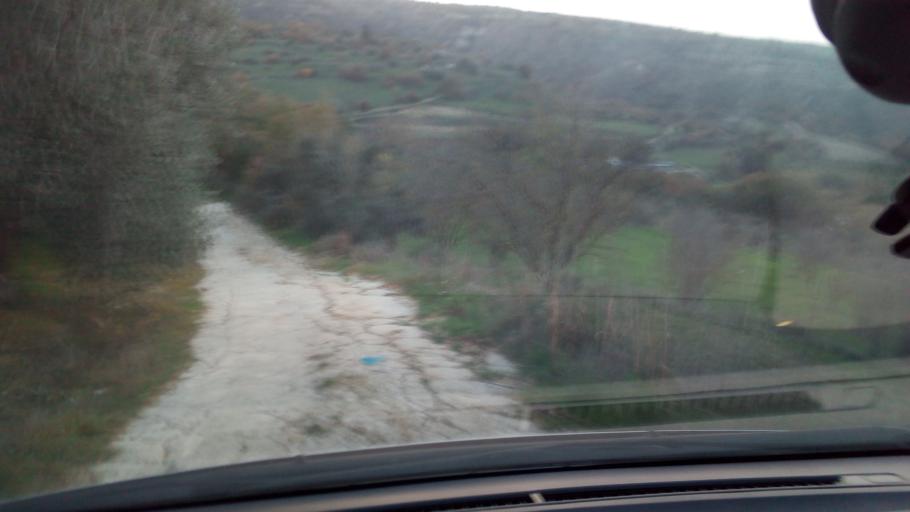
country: CY
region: Pafos
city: Polis
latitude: 34.9524
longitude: 32.4698
